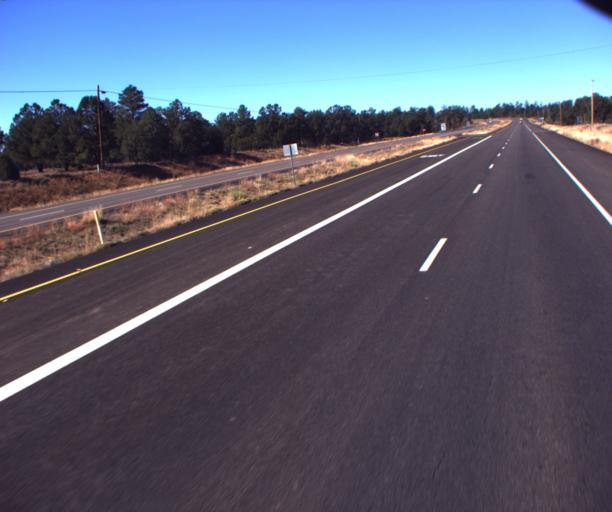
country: US
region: Arizona
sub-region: Apache County
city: Saint Michaels
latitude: 35.6645
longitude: -109.1612
